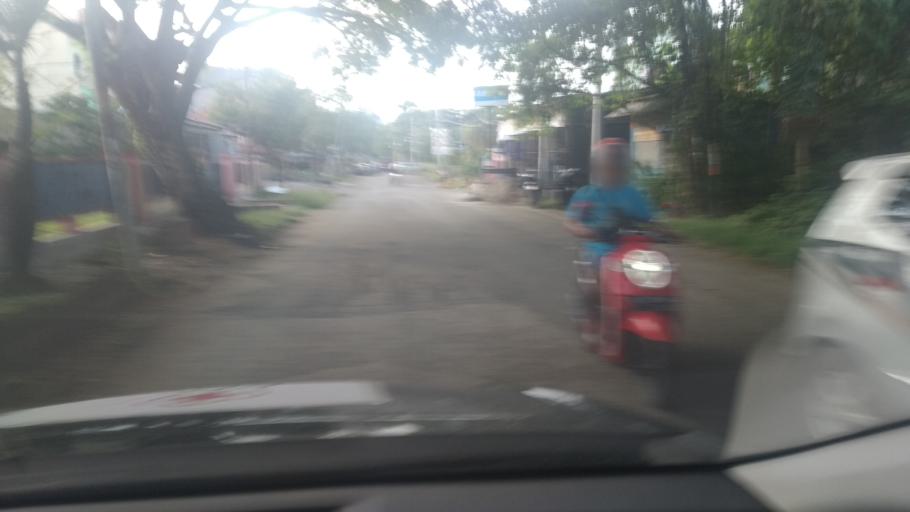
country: ID
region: Sulawesi Barat
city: Mamuju
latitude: -2.6763
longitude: 118.8886
